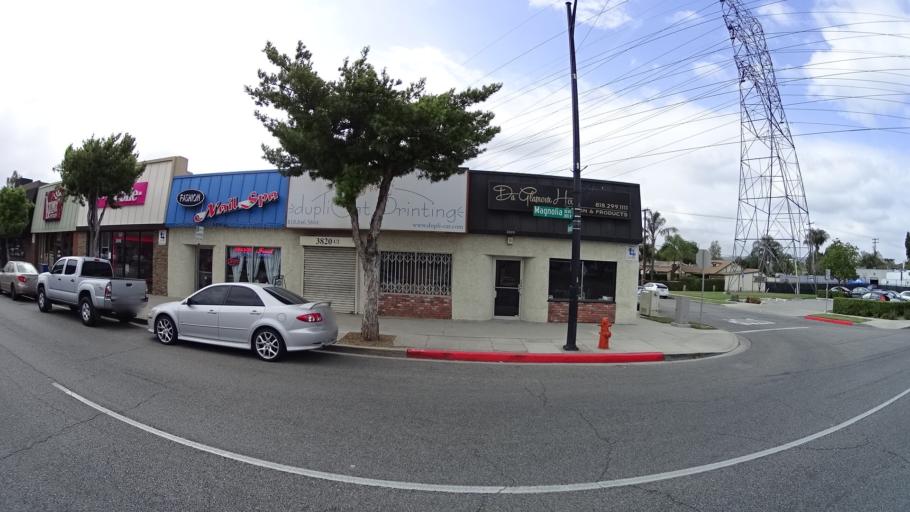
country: US
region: California
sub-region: Los Angeles County
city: Universal City
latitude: 34.1672
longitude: -118.3488
